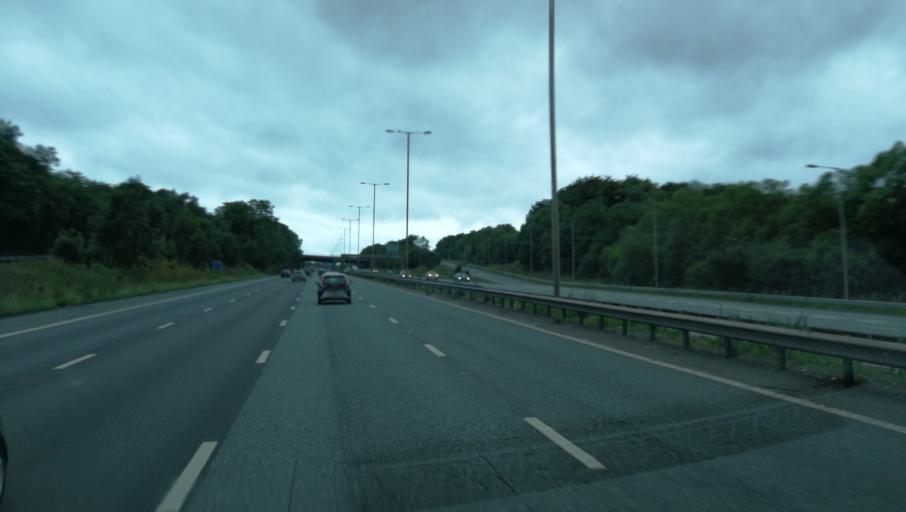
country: GB
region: England
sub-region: Manchester
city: Swinton
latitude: 53.5276
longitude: -2.3305
